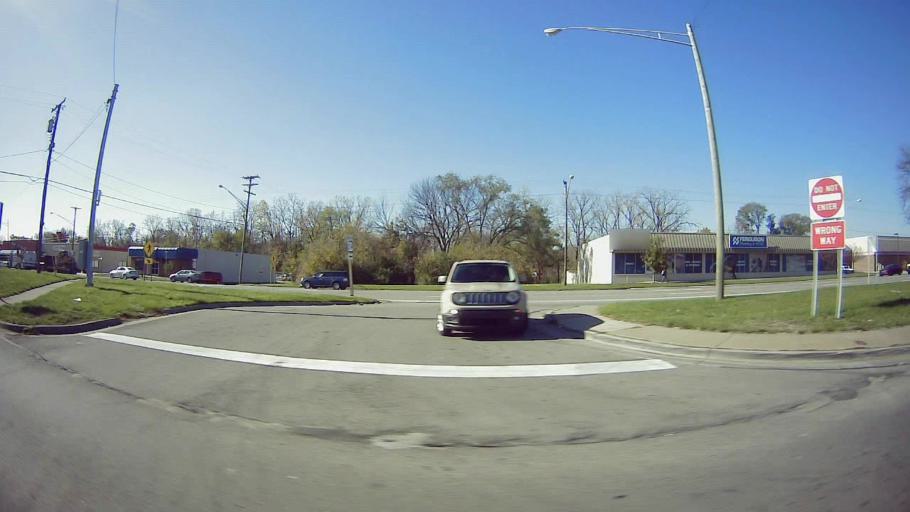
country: US
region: Michigan
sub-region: Wayne County
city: Redford
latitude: 42.3981
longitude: -83.2764
